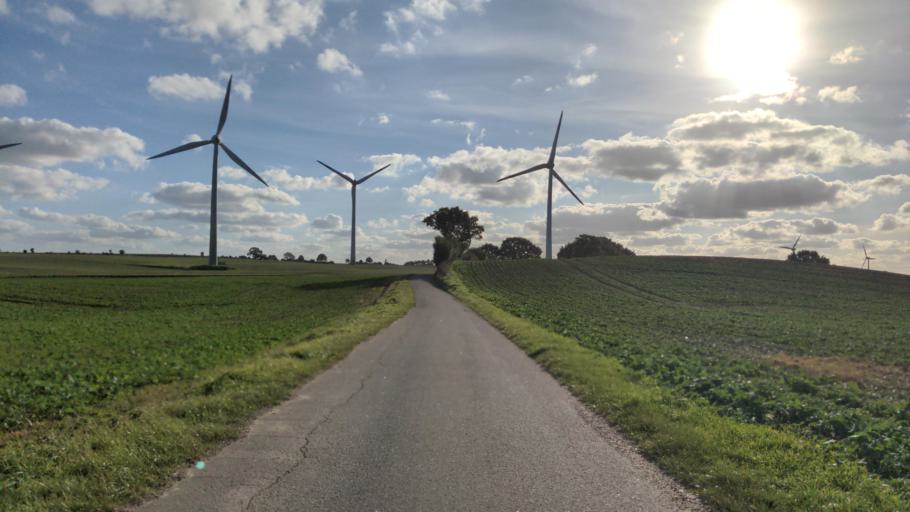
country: DE
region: Schleswig-Holstein
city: Schashagen
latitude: 54.1496
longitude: 10.9107
